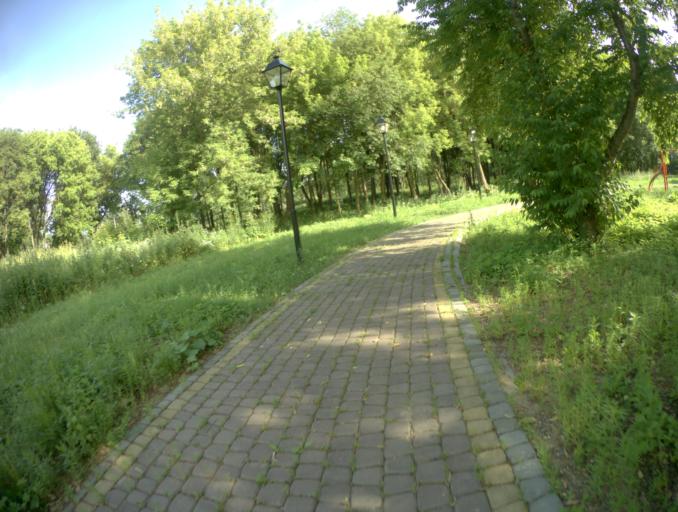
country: RU
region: Vladimir
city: Suzdal'
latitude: 56.4300
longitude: 40.4478
